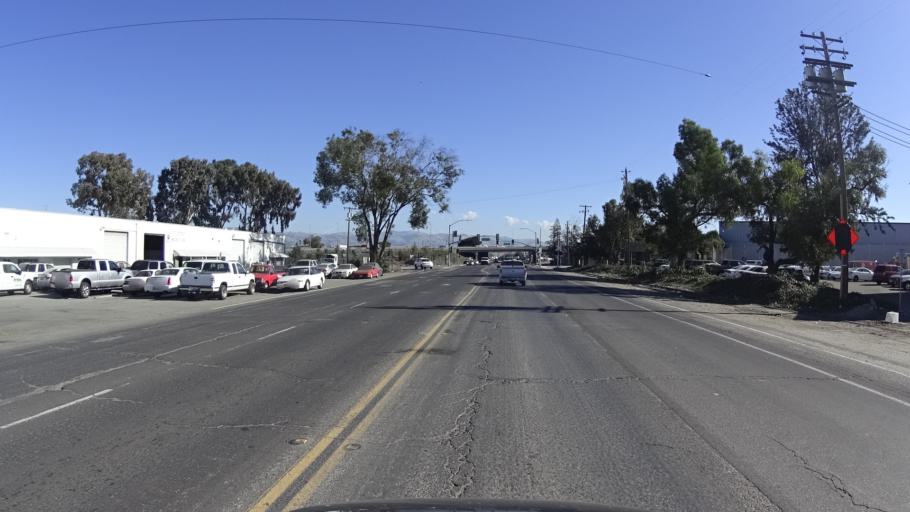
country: US
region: California
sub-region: Santa Clara County
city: San Jose
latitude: 37.3680
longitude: -121.9041
